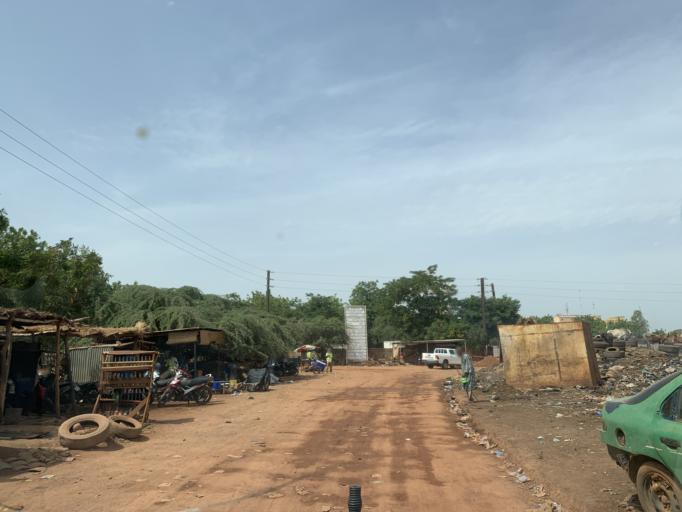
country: BF
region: Centre
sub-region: Kadiogo Province
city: Ouagadougou
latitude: 12.3363
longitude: -1.5153
